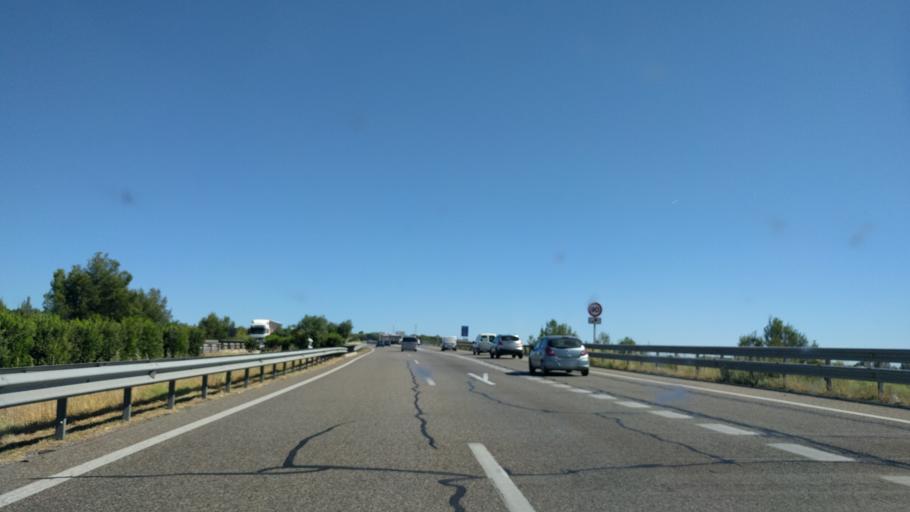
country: ES
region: Catalonia
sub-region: Provincia de Lleida
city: Alcoletge
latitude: 41.6466
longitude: 0.6722
